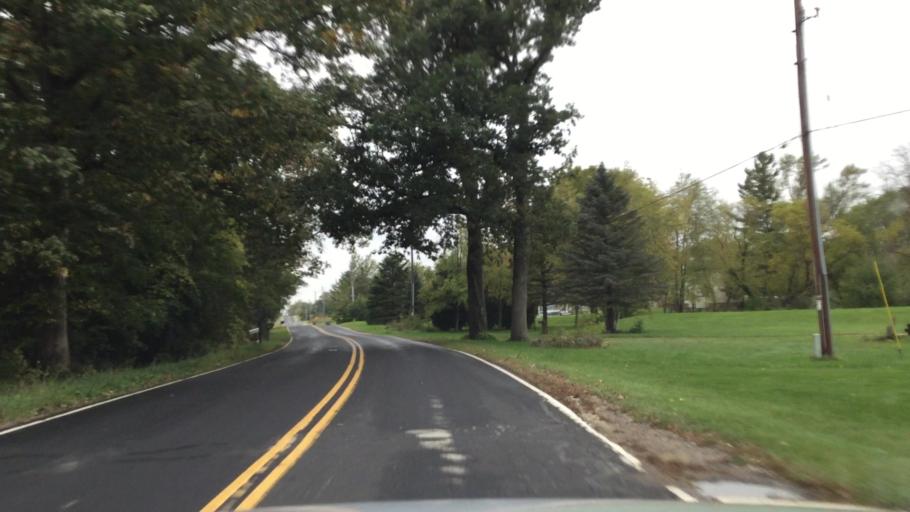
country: US
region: Wisconsin
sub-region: Racine County
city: Waterford
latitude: 42.7639
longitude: -88.1677
